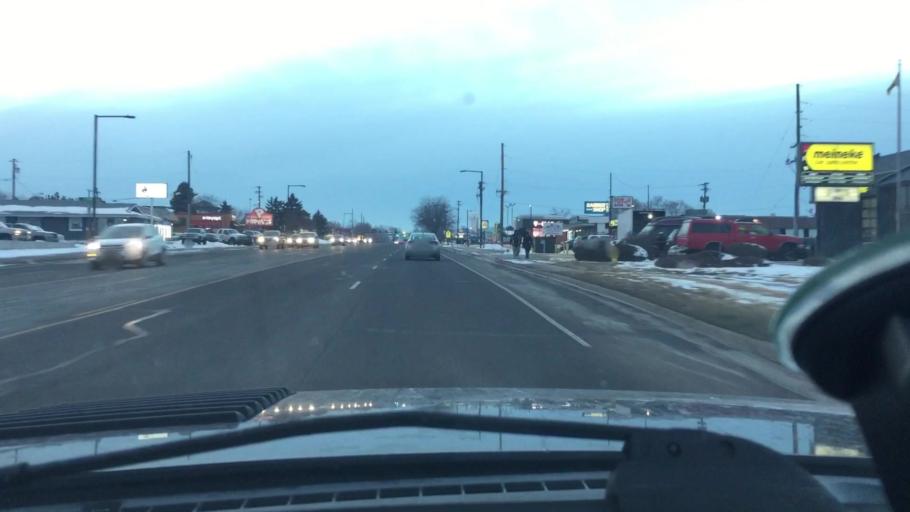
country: US
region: Colorado
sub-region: Adams County
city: Federal Heights
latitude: 39.8491
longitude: -104.9919
